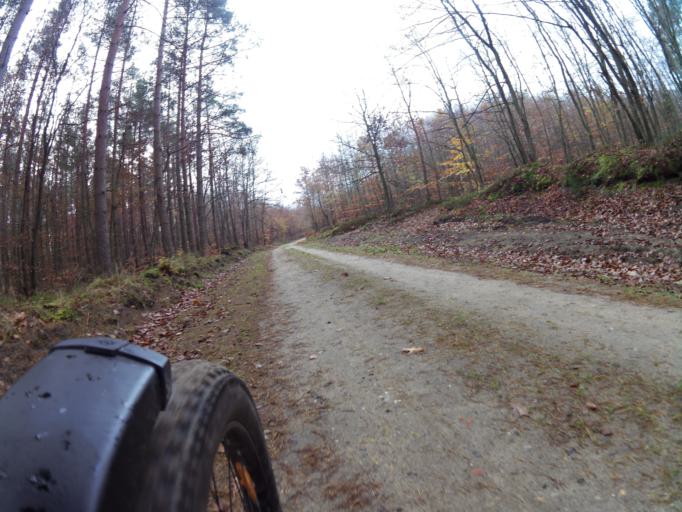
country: PL
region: Pomeranian Voivodeship
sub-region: Powiat pucki
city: Krokowa
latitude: 54.7774
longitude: 18.0919
